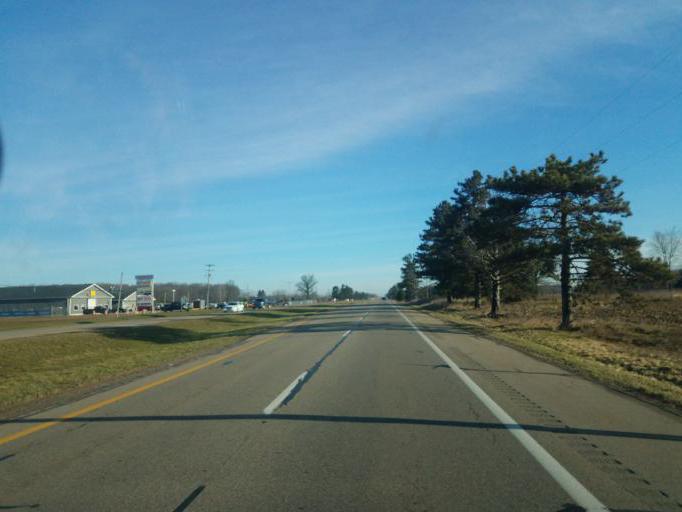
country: US
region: Michigan
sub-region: Clinton County
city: Saint Johns
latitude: 43.0621
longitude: -84.5638
